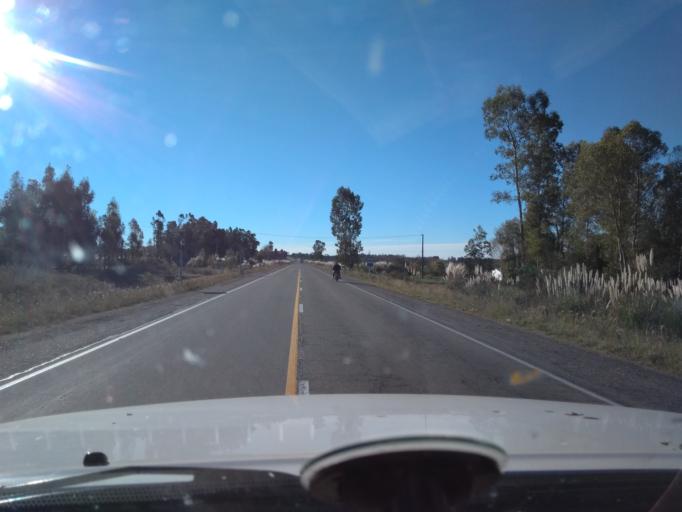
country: UY
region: Canelones
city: Sauce
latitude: -34.6061
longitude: -56.0487
